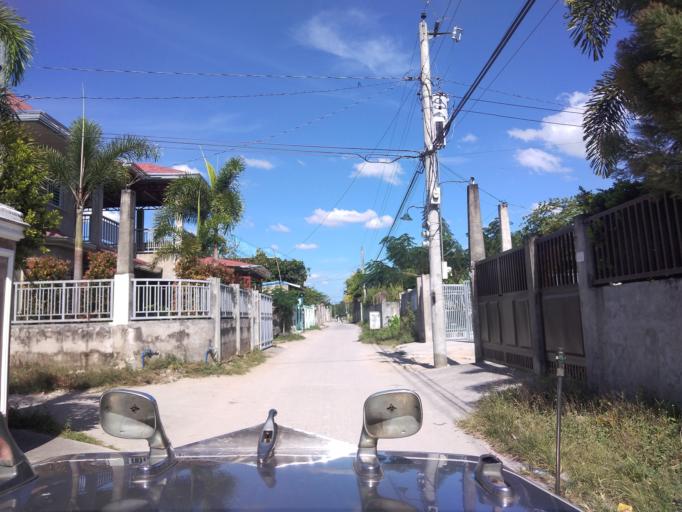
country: PH
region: Central Luzon
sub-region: Province of Pampanga
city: San Agustin
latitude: 14.9936
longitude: 120.6091
